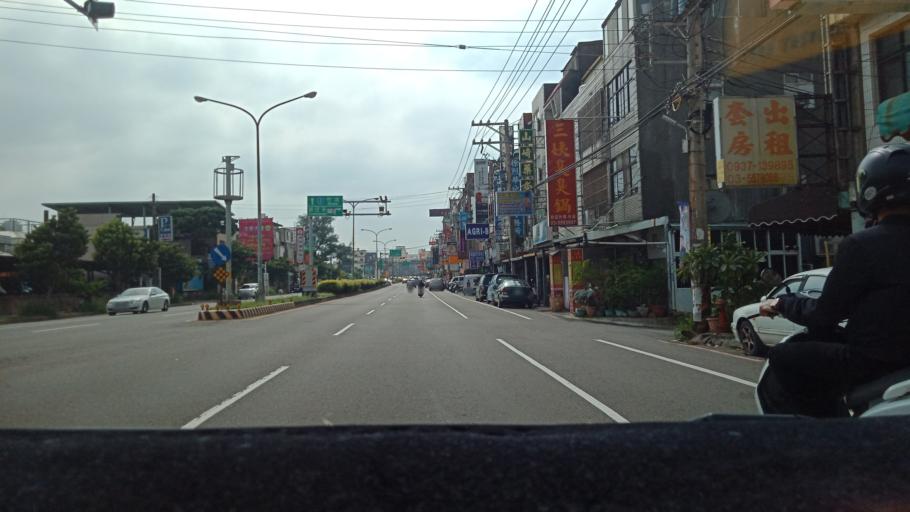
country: TW
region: Taiwan
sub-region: Hsinchu
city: Zhubei
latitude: 24.8710
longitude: 120.9978
